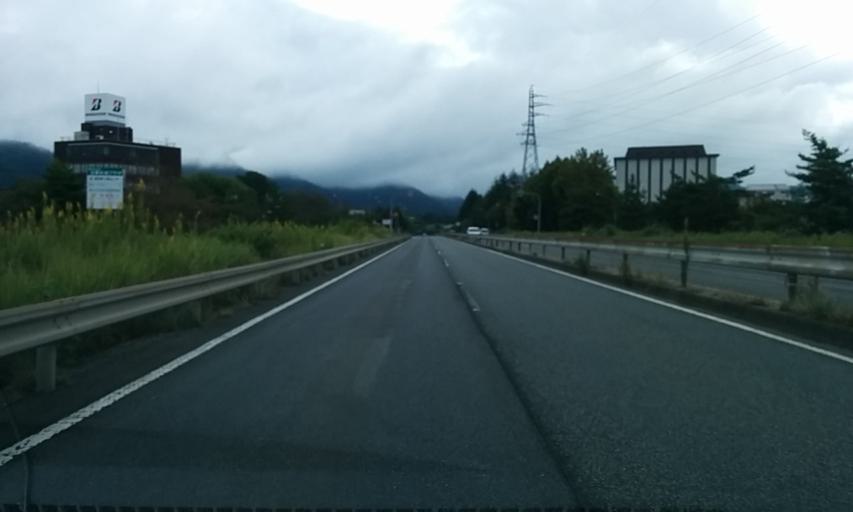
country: JP
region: Kyoto
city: Fukuchiyama
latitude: 35.2845
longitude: 135.1716
